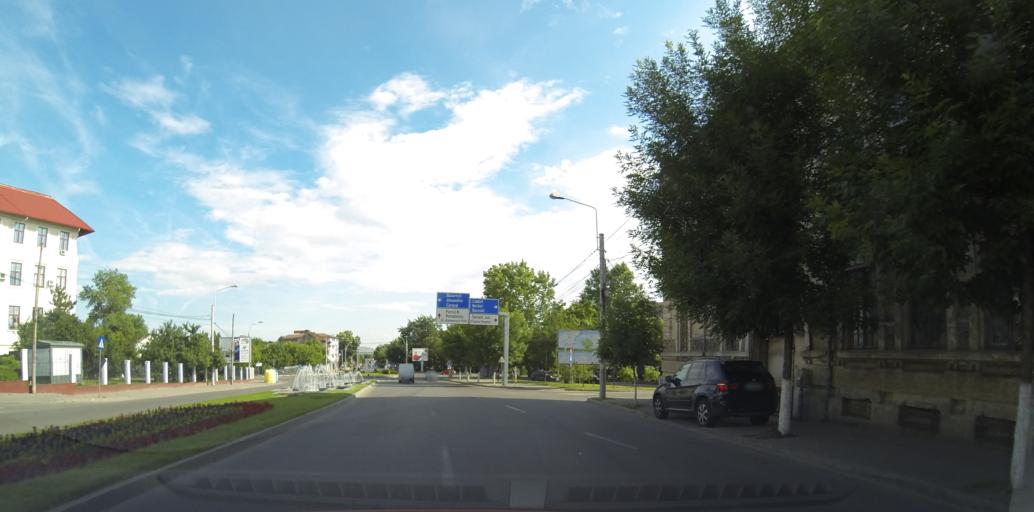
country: RO
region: Dolj
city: Craiova
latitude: 44.3093
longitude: 23.7965
